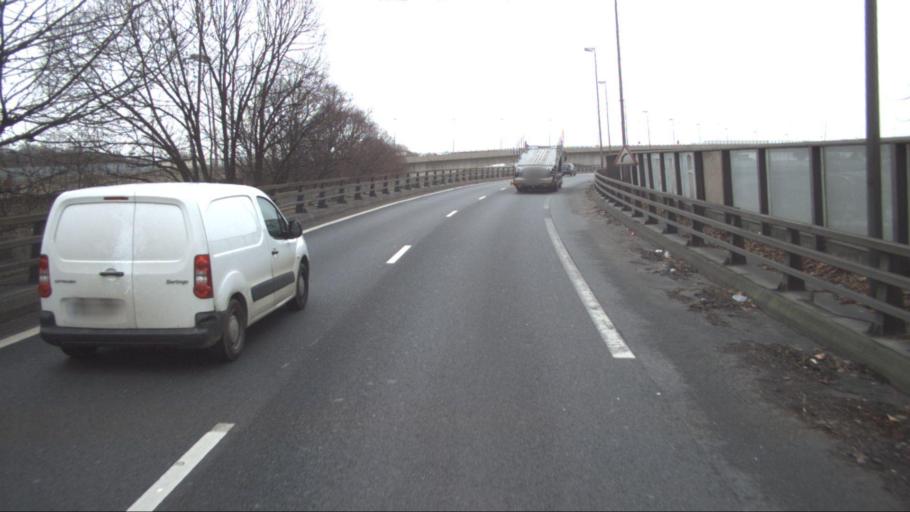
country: FR
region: Ile-de-France
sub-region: Departement du Val-de-Marne
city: Maisons-Alfort
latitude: 48.8167
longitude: 2.4443
